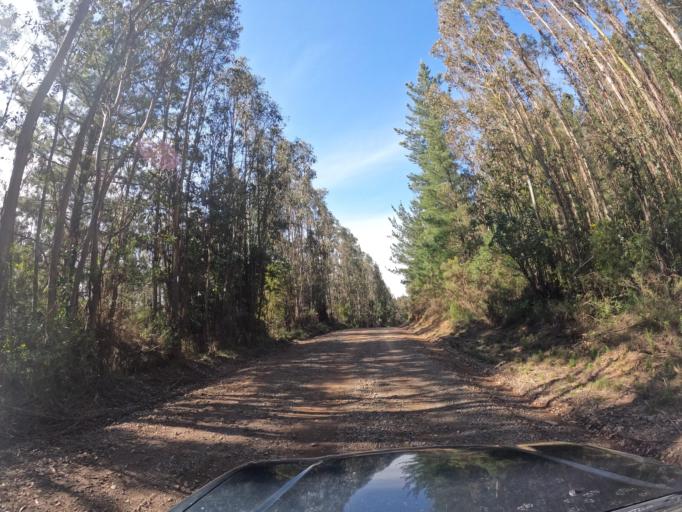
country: CL
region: Biobio
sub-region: Provincia de Biobio
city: La Laja
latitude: -37.0850
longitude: -72.7888
